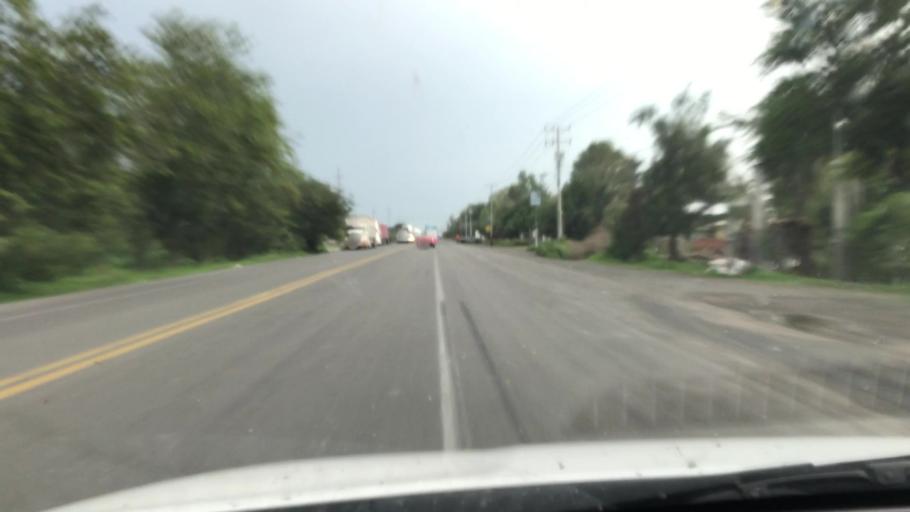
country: MX
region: Michoacan
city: Tanhuato de Guerrero
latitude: 20.2795
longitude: -102.3669
